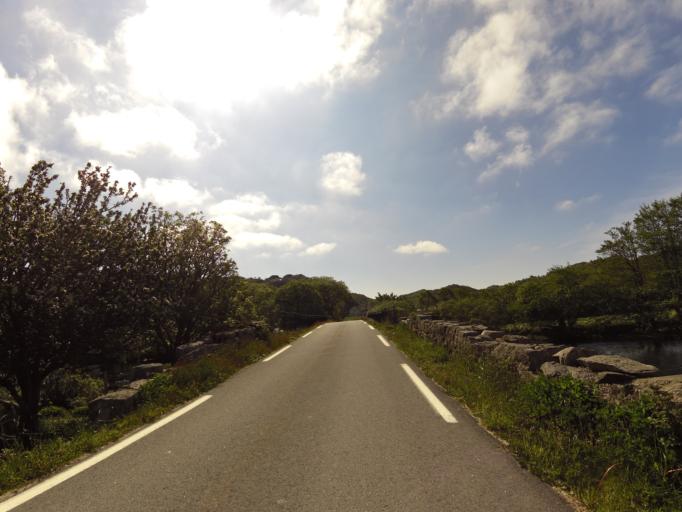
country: NO
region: Rogaland
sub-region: Ha
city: Vigrestad
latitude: 58.5175
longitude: 5.8209
